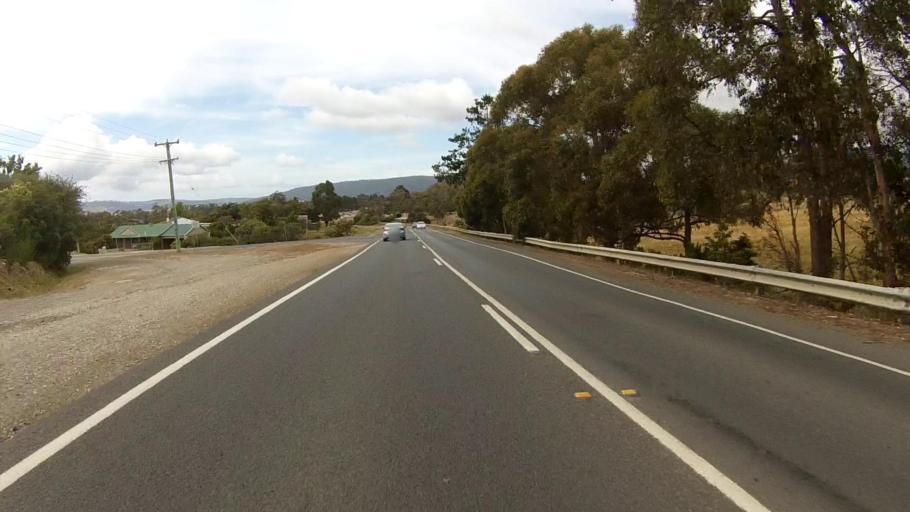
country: AU
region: Tasmania
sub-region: Kingborough
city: Margate
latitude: -43.0302
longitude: 147.2640
